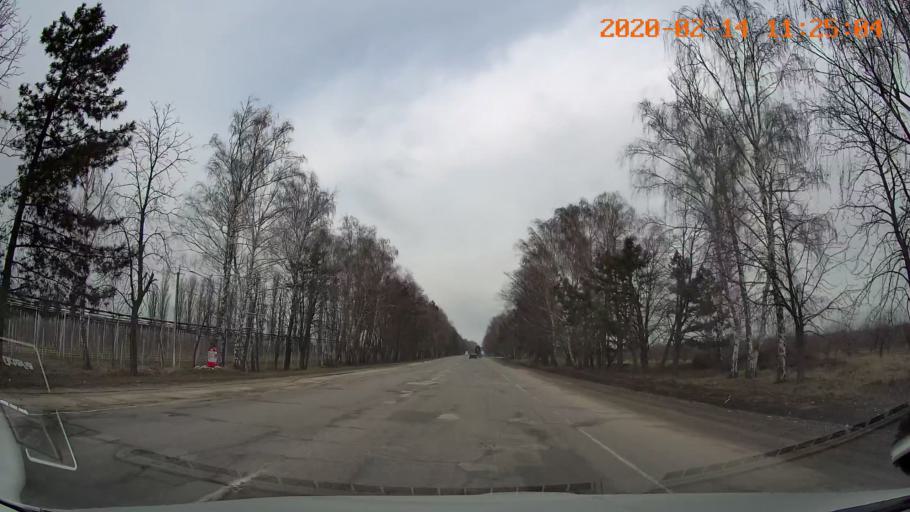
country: MD
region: Briceni
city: Briceni
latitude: 48.3453
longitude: 27.1075
